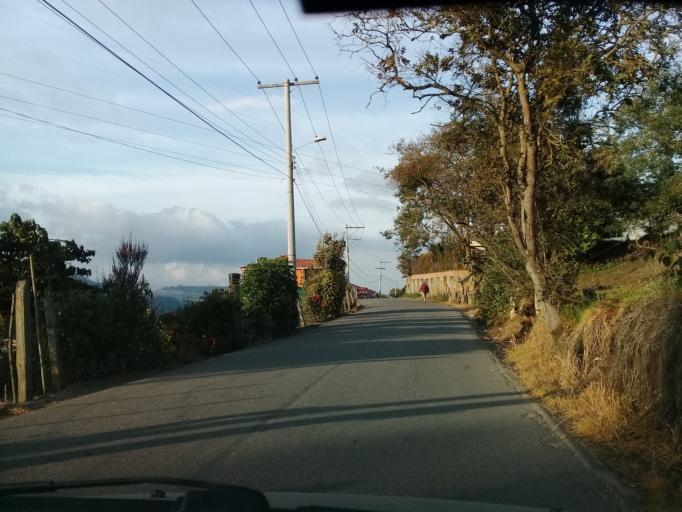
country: CO
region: Cundinamarca
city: Sibate
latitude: 4.4616
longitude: -74.2659
